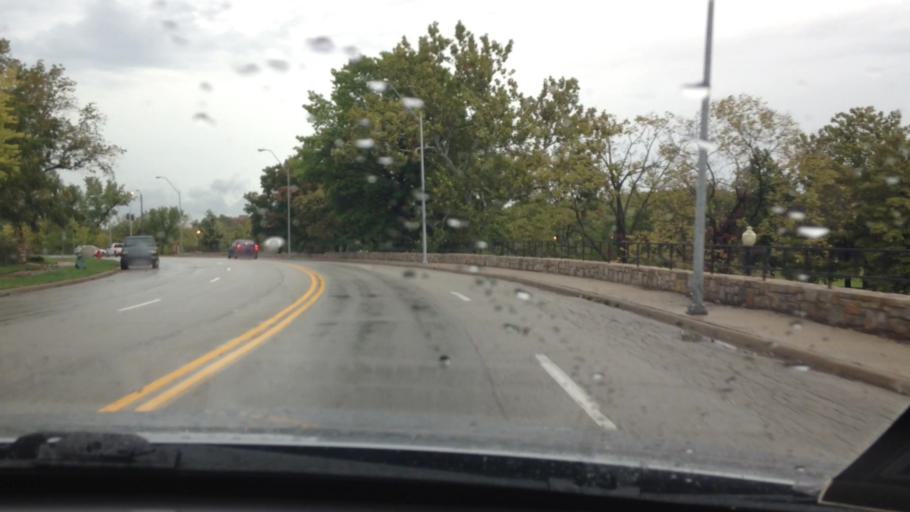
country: US
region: Missouri
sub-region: Jackson County
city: Kansas City
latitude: 39.0760
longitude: -94.5654
